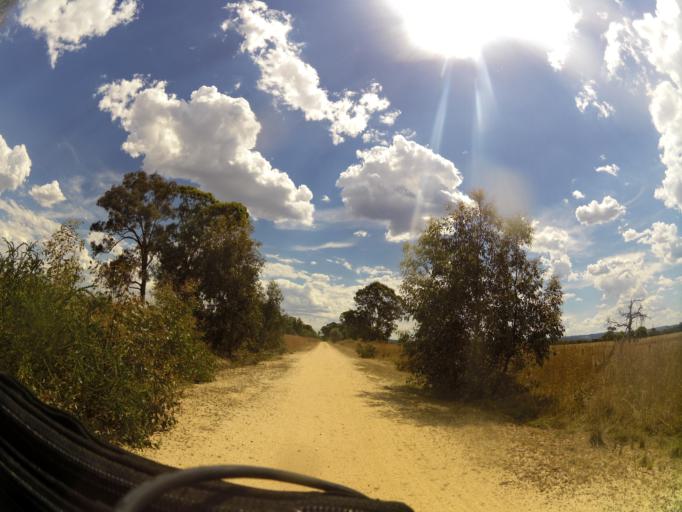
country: AU
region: Victoria
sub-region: Wellington
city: Heyfield
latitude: -37.9806
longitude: 146.7390
